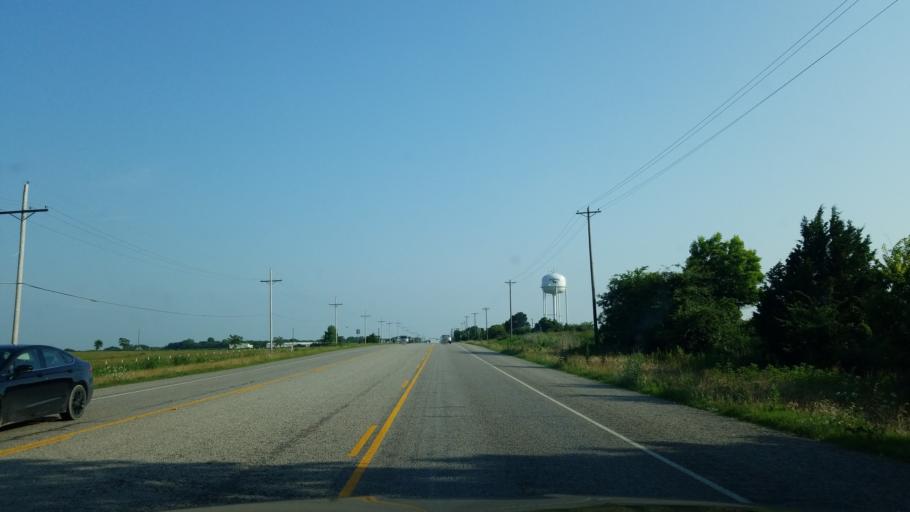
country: US
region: Texas
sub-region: Denton County
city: Pilot Point
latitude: 33.3747
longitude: -96.9632
